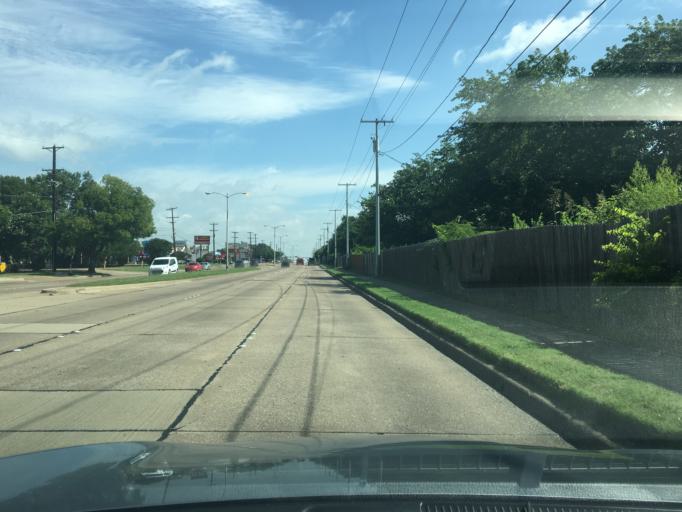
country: US
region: Texas
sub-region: Dallas County
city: Richardson
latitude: 32.9118
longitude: -96.7003
